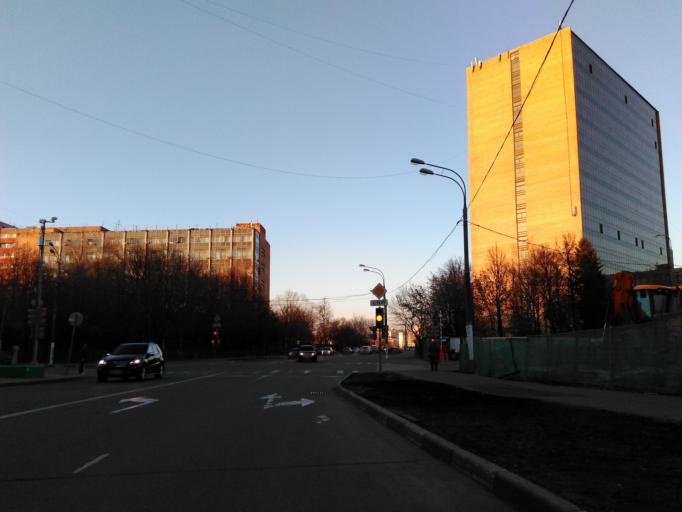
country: RU
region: Moskovskaya
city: Cheremushki
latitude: 55.6454
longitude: 37.5438
